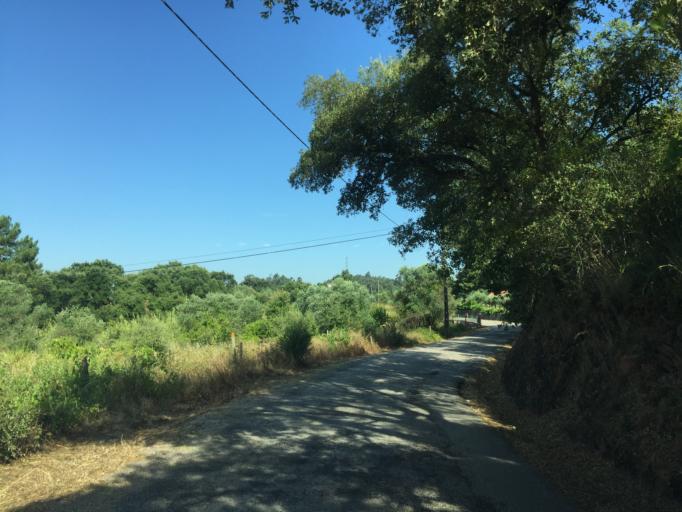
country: PT
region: Santarem
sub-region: Tomar
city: Tomar
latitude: 39.6554
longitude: -8.3742
